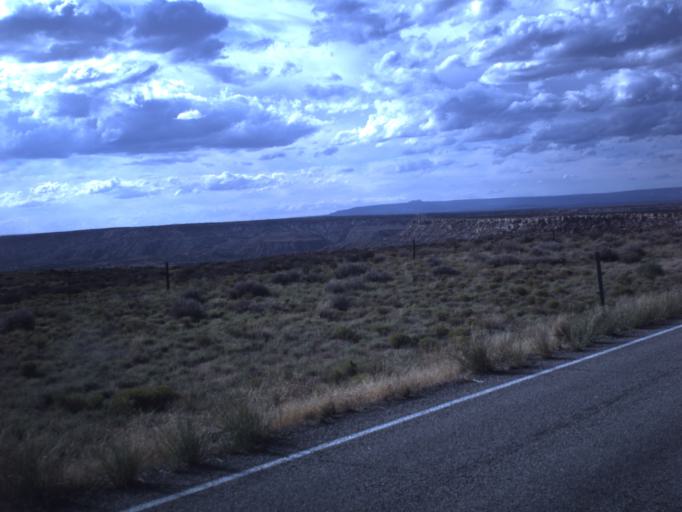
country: US
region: Utah
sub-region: San Juan County
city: Blanding
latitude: 37.3320
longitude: -109.3461
